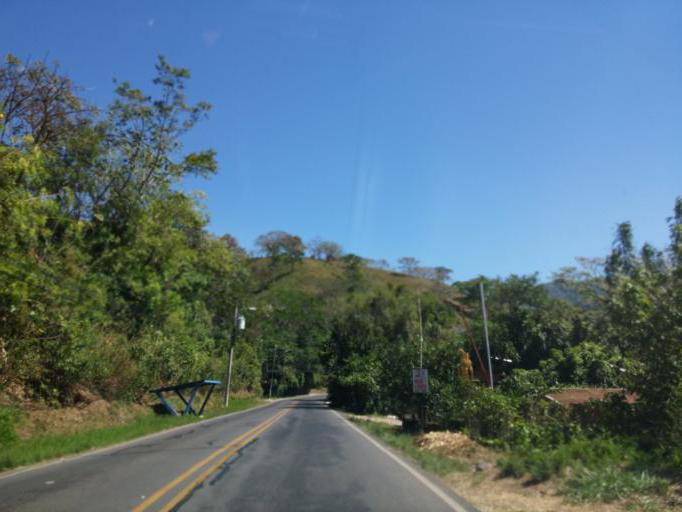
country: CR
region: Heredia
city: Colon
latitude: 9.8938
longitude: -84.2302
